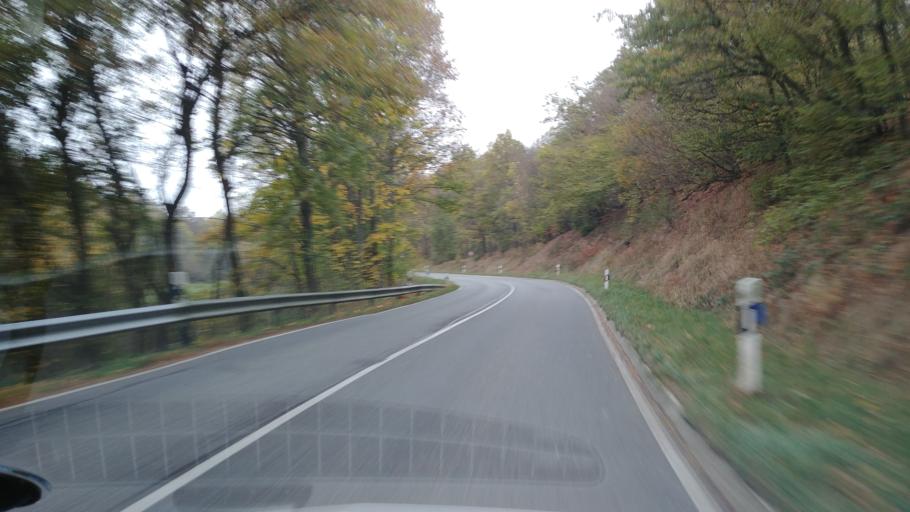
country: DE
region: Hesse
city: Taunusstein
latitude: 50.1541
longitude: 8.1582
